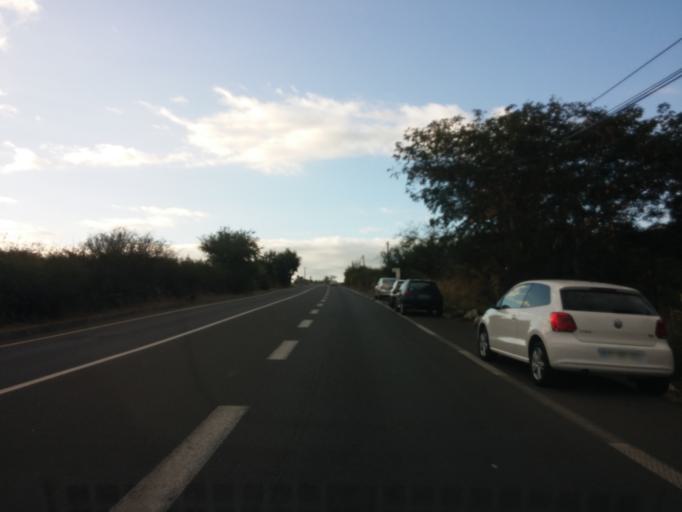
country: RE
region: Reunion
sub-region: Reunion
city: Saint-Paul
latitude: -21.0448
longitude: 55.2403
